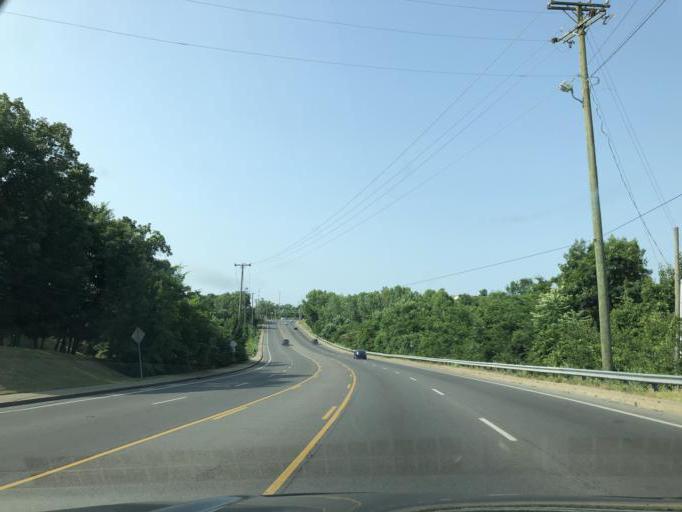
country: US
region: Tennessee
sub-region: Rutherford County
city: La Vergne
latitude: 36.0590
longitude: -86.6414
